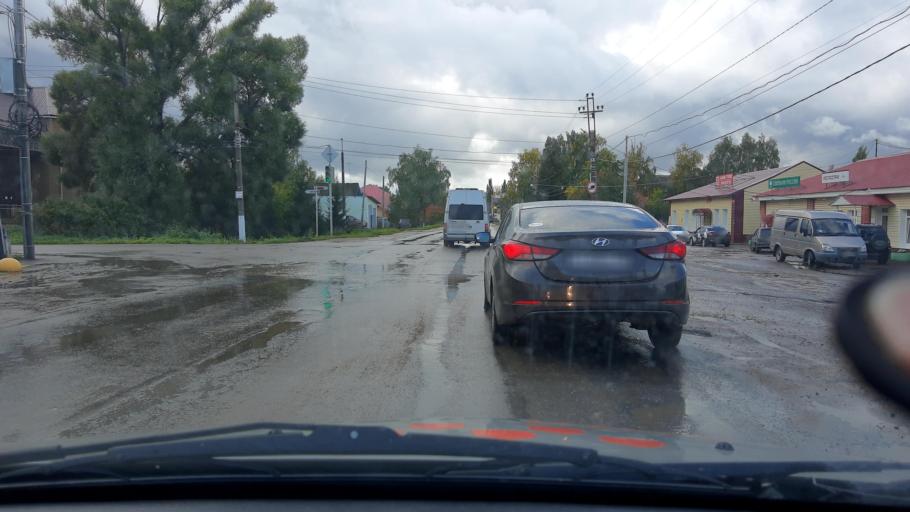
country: RU
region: Bashkortostan
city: Iglino
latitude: 54.8379
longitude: 56.4230
